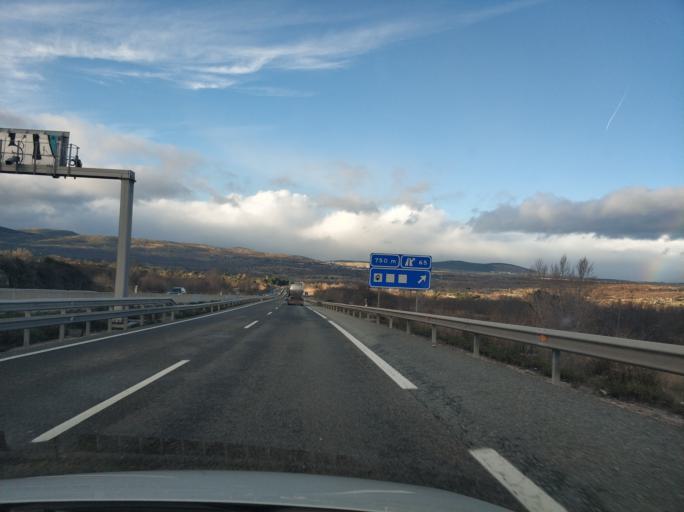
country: ES
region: Madrid
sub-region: Provincia de Madrid
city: La Cabrera
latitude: 40.8952
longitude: -3.6034
